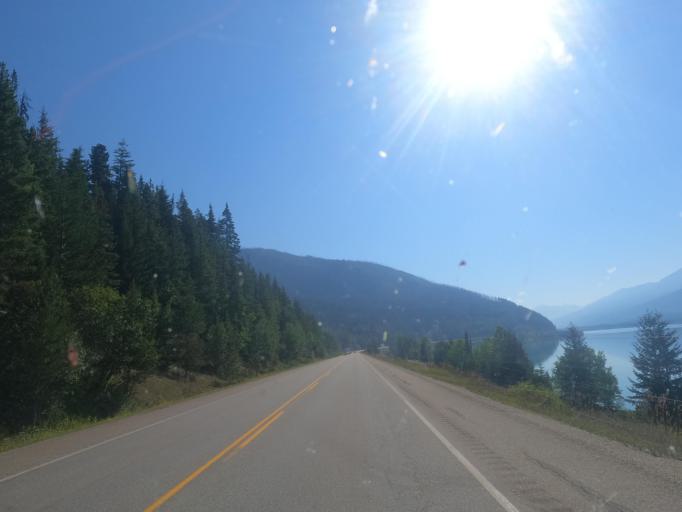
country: CA
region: Alberta
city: Jasper Park Lodge
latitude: 52.9536
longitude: -118.8776
